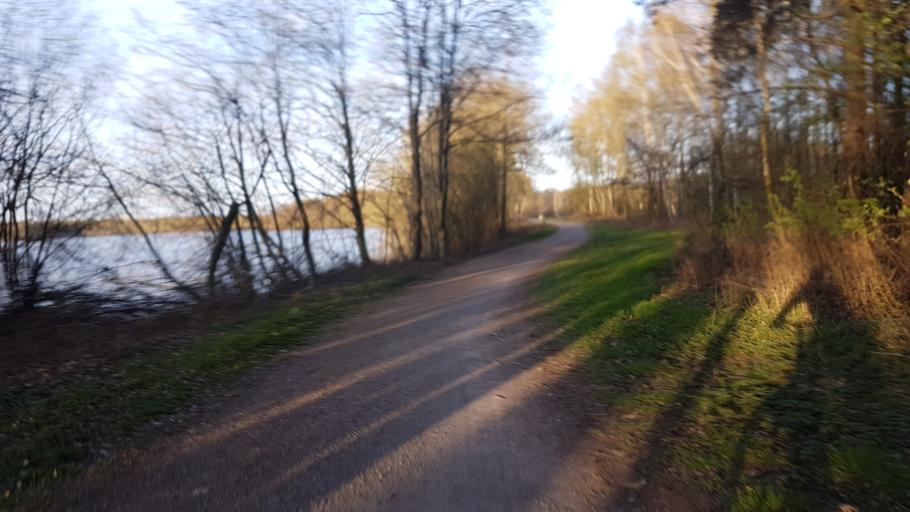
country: DE
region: Lower Saxony
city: Isernhagen Farster Bauerschaft
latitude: 52.4201
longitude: 9.8513
